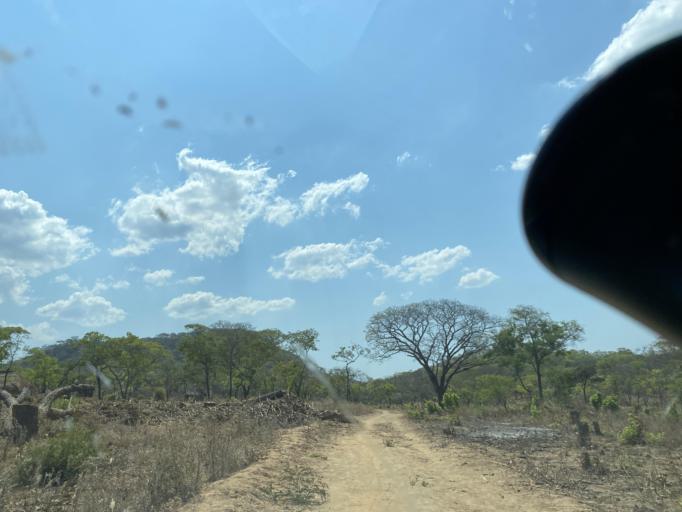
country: ZM
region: Lusaka
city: Chongwe
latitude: -15.0828
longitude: 29.4714
